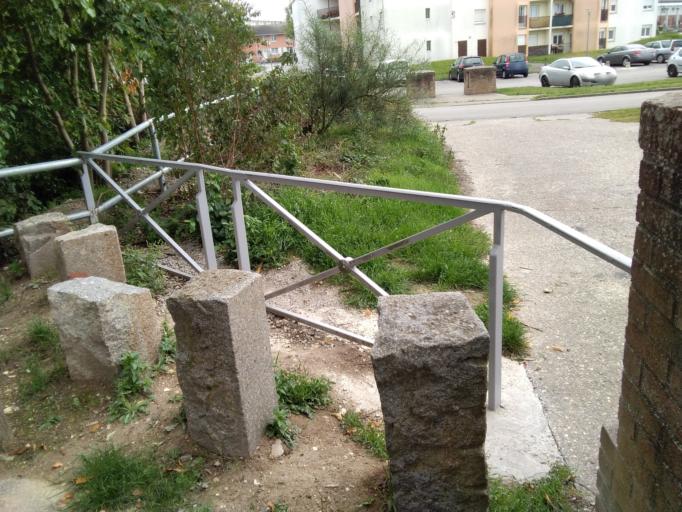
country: FR
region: Picardie
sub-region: Departement de la Somme
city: Amiens
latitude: 49.9175
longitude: 2.2963
